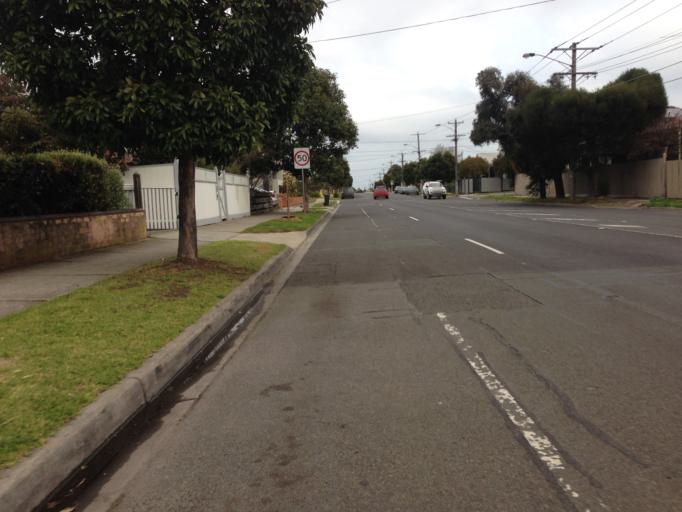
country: AU
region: Victoria
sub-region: Darebin
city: Thornbury
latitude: -37.7650
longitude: 145.0123
